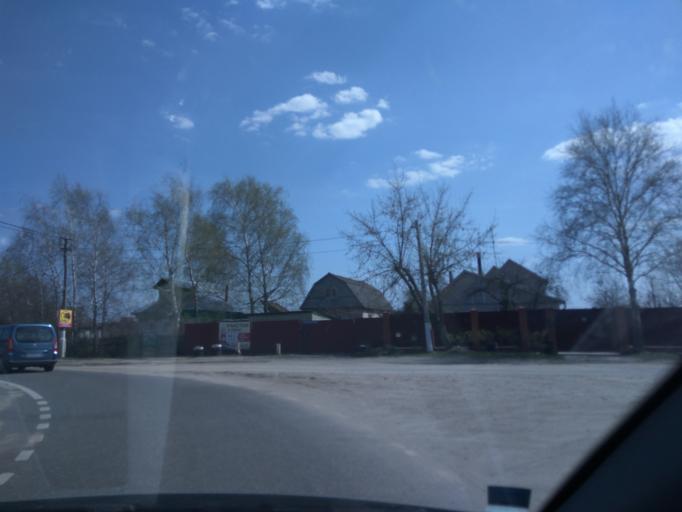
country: RU
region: Moskovskaya
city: Ramenskoye
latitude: 55.5441
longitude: 38.2351
